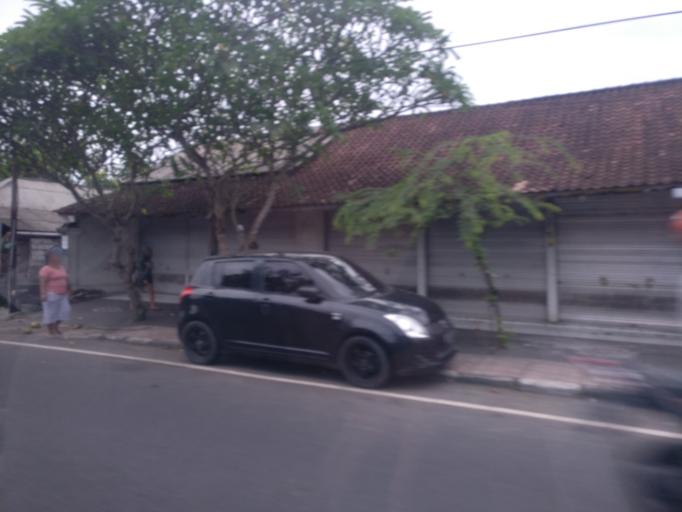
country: ID
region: Bali
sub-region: Kabupaten Gianyar
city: Ubud
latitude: -8.5590
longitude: 115.3017
